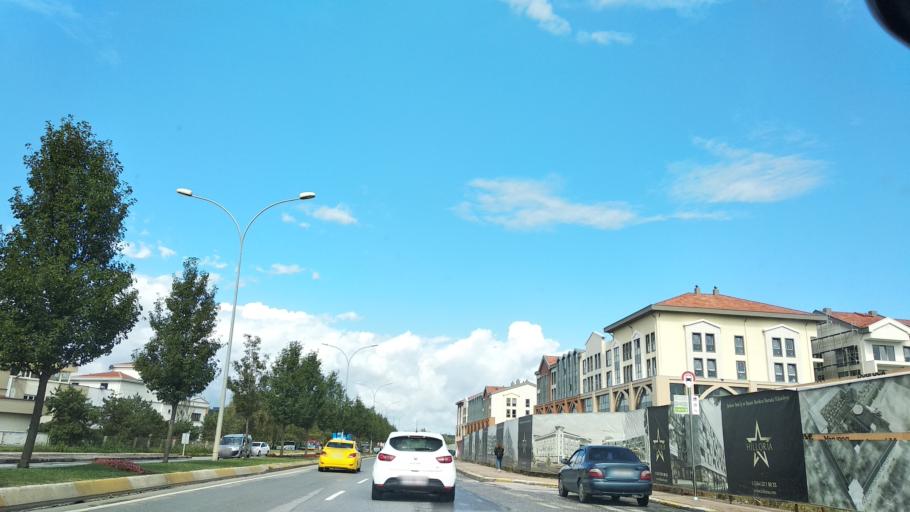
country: TR
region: Sakarya
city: Adapazari
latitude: 40.7731
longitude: 30.3642
